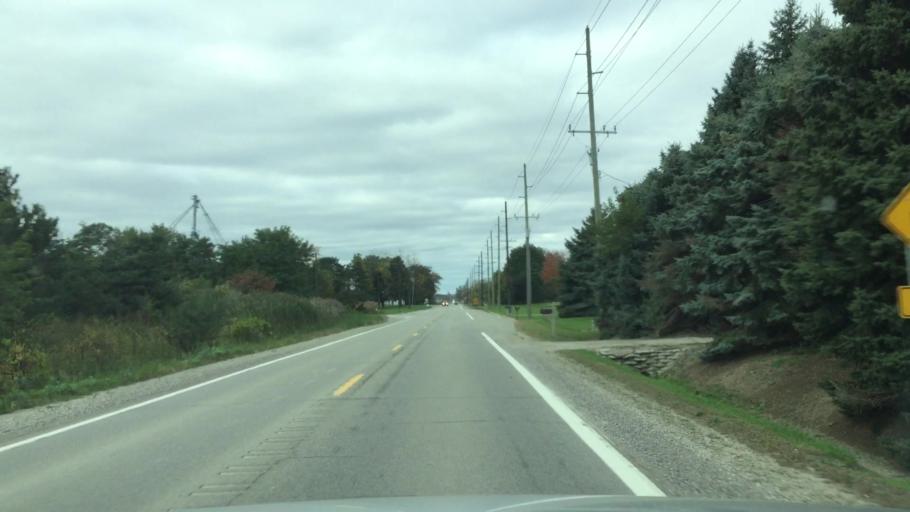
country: US
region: Michigan
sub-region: Macomb County
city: Richmond
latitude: 42.8085
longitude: -82.7899
